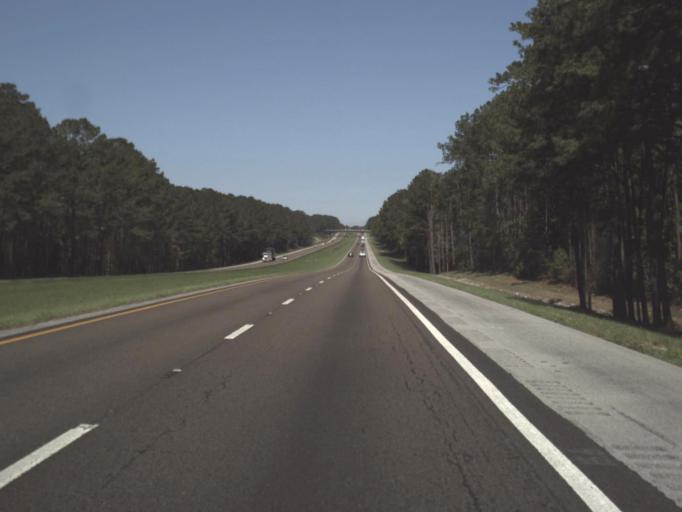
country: US
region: Florida
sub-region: Walton County
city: DeFuniak Springs
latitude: 30.6995
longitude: -86.1538
